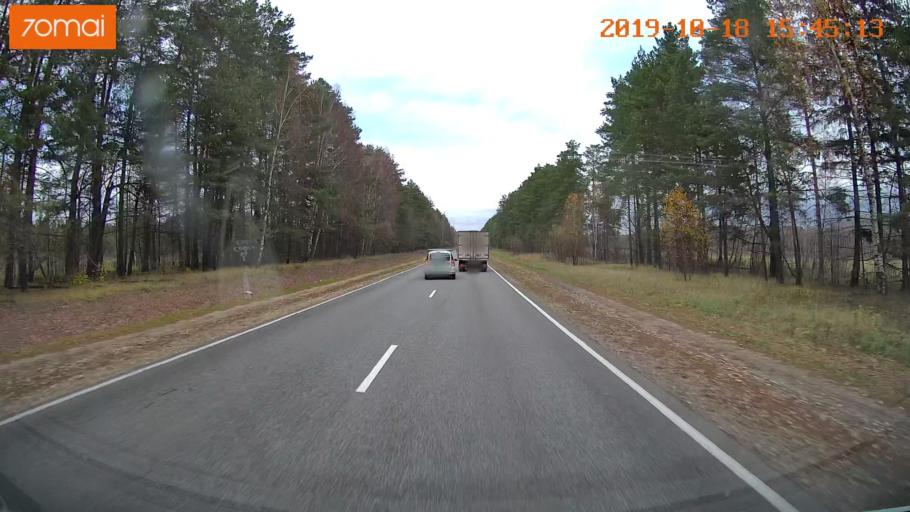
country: RU
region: Vladimir
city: Golovino
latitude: 55.9904
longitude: 40.5587
